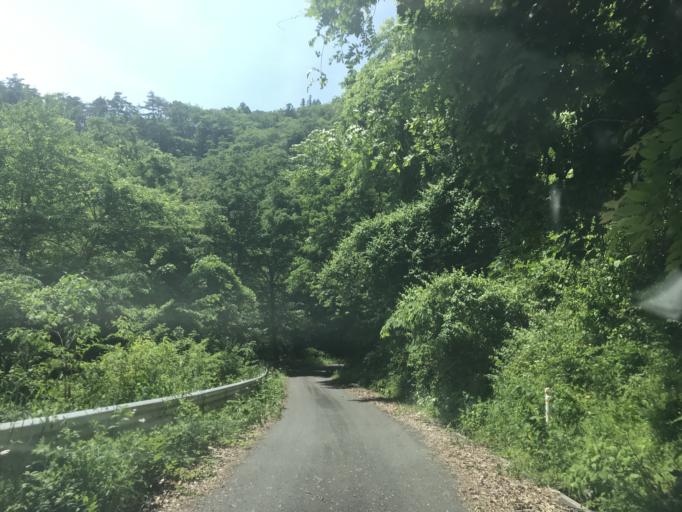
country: JP
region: Iwate
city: Ichinoseki
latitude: 38.9530
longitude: 141.2433
